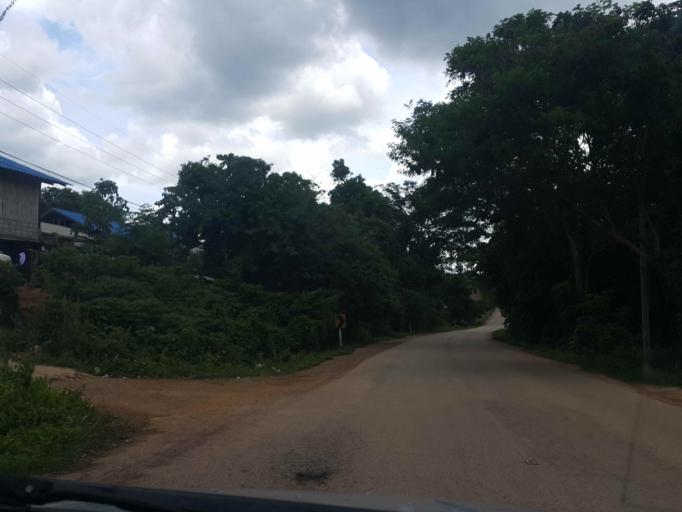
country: TH
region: Lampang
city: Ngao
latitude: 18.9509
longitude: 100.0764
